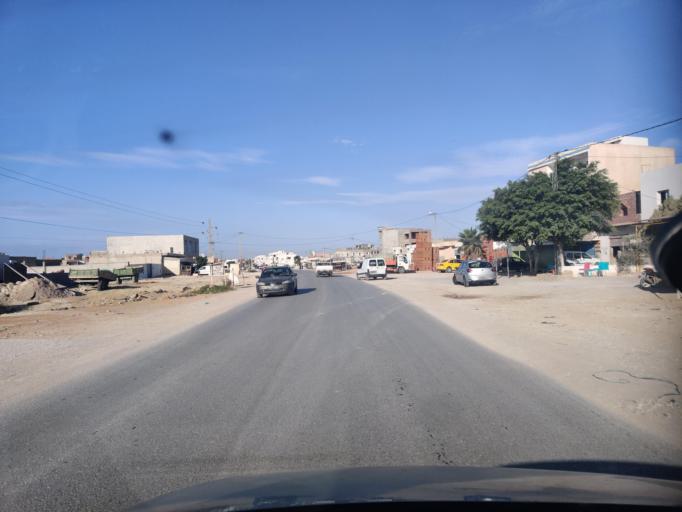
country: TN
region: Ariana
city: Ariana
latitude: 36.9571
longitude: 10.2056
